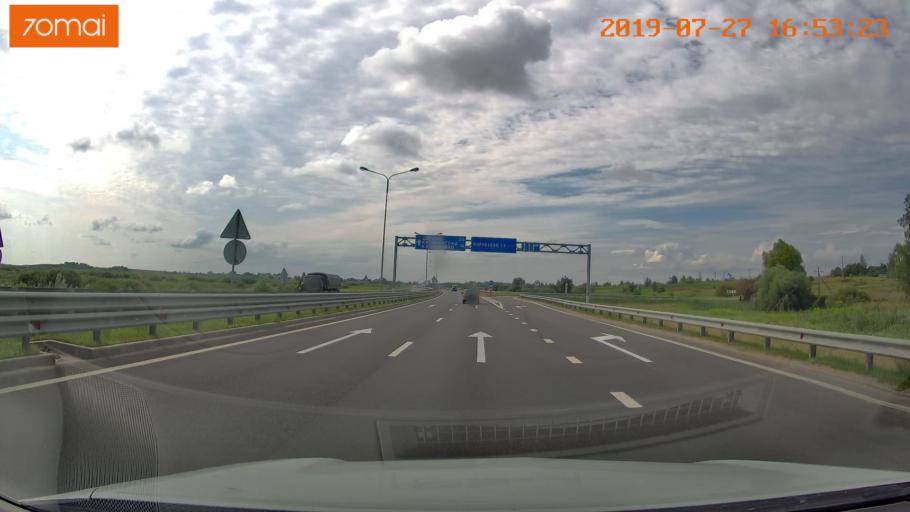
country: RU
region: Kaliningrad
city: Bol'shoe Isakovo
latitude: 54.6876
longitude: 20.8333
